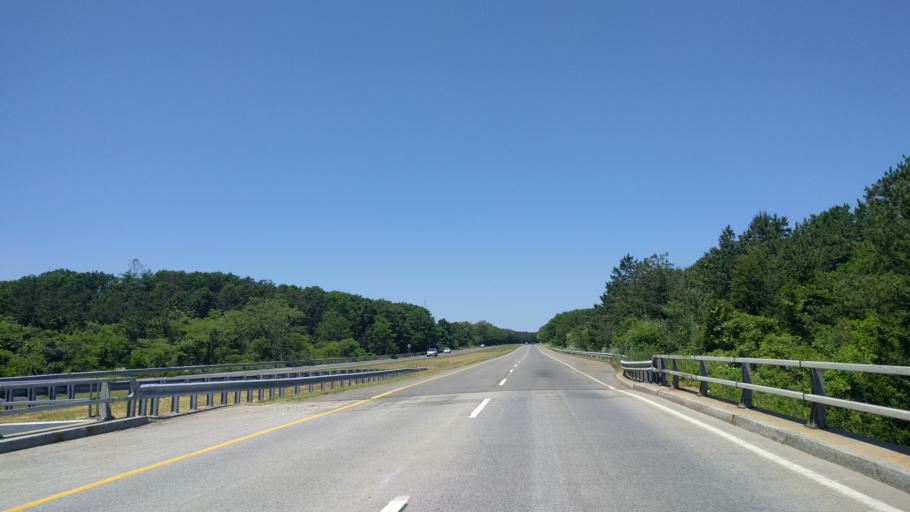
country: US
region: New York
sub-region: Suffolk County
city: Eastport
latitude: 40.8486
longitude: -72.7400
